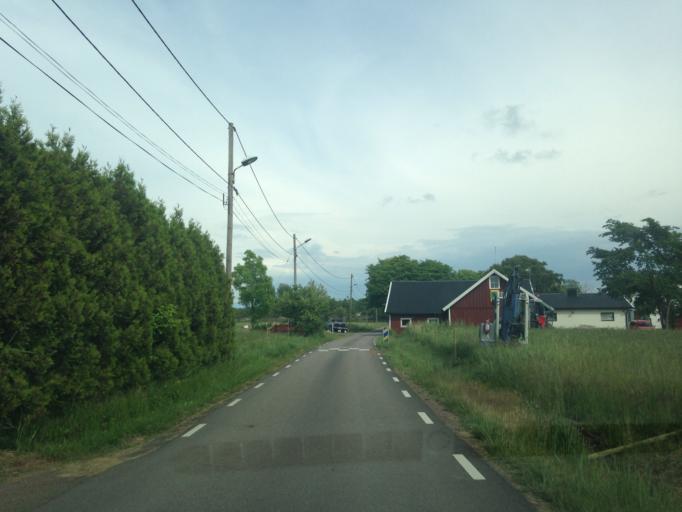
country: SE
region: Vaestra Goetaland
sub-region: Goteborg
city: Majorna
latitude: 57.7593
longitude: 11.8565
